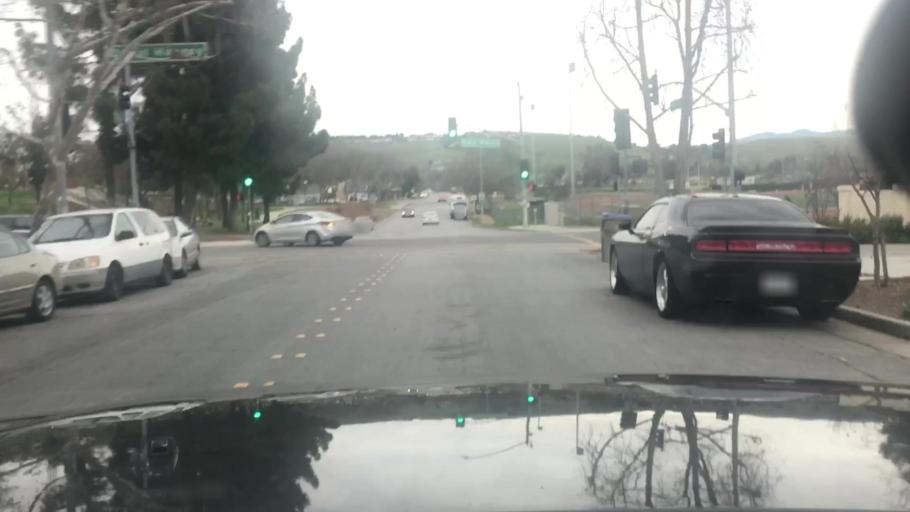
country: US
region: California
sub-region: Santa Clara County
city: Seven Trees
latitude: 37.3073
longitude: -121.8038
